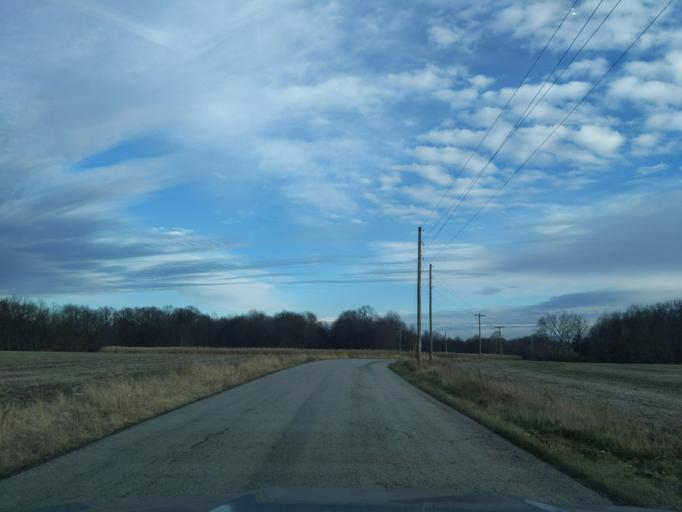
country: US
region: Indiana
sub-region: Decatur County
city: Greensburg
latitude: 39.2149
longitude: -85.4507
